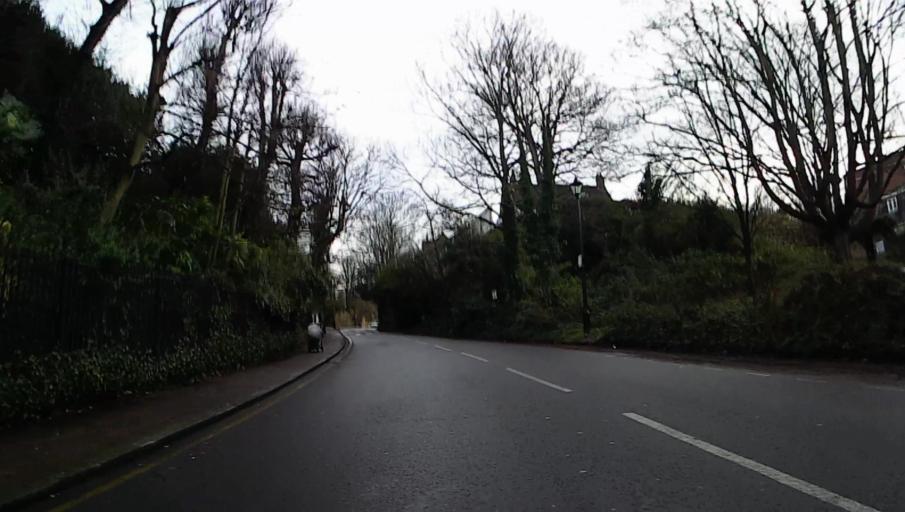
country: GB
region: England
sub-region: Greater London
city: Blackheath
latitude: 51.4762
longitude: -0.0054
